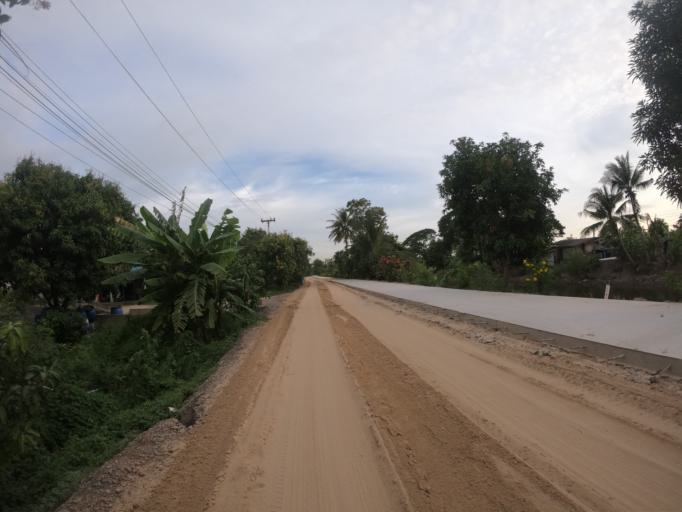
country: TH
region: Pathum Thani
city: Ban Rangsit
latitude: 14.0230
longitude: 100.8002
